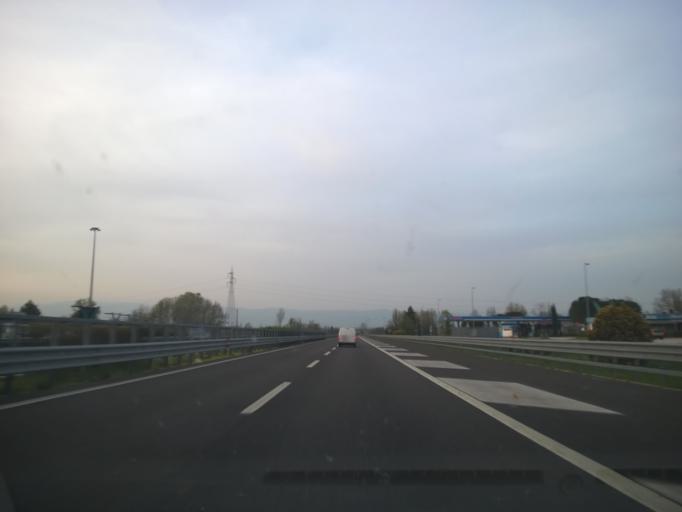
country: IT
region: Veneto
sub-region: Provincia di Vicenza
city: Vigardolo
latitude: 45.5940
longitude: 11.5992
